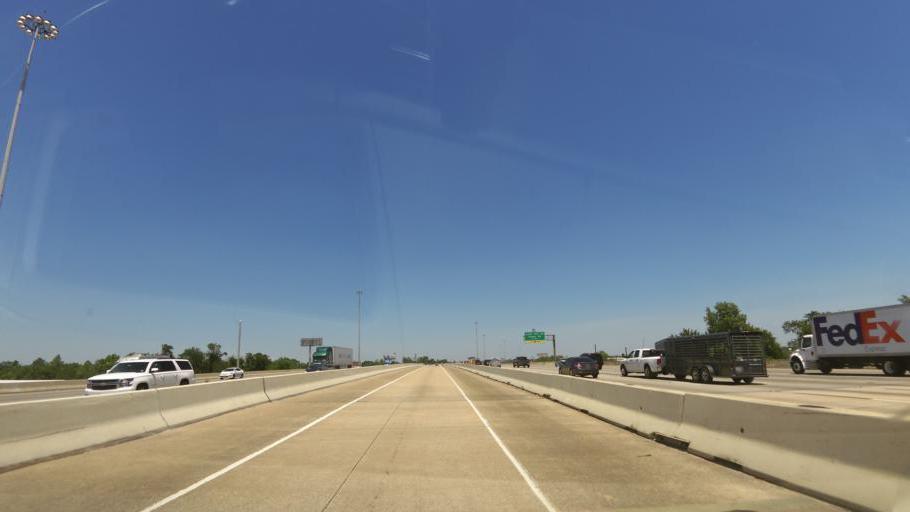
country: US
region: Texas
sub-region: Harris County
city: Aldine
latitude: 29.8586
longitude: -95.3335
